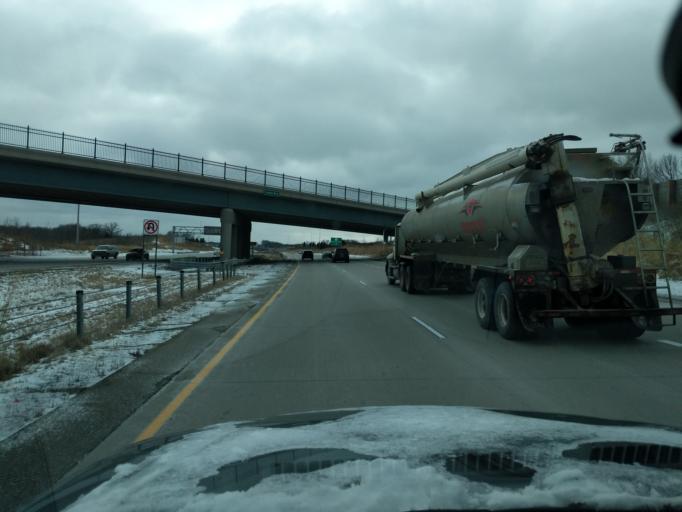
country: US
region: Minnesota
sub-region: Carver County
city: Chanhassen
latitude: 44.8413
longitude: -93.5450
